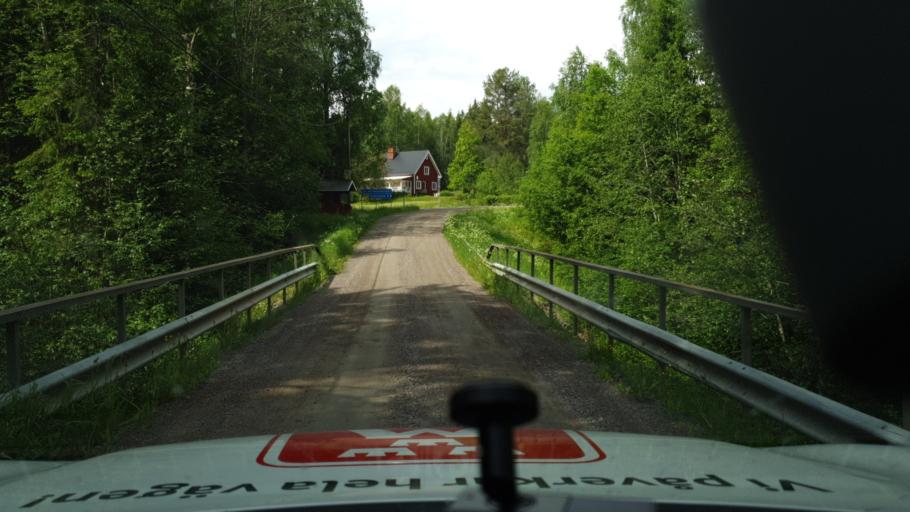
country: SE
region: Vaermland
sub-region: Torsby Kommun
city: Torsby
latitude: 59.9834
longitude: 12.8321
